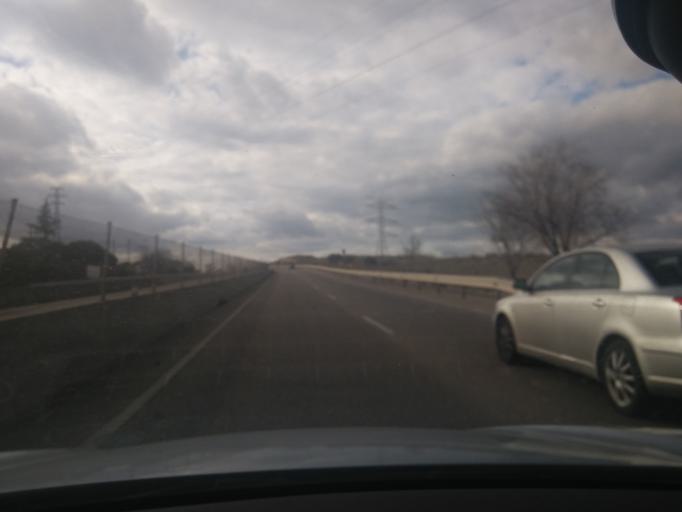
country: ES
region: Madrid
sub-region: Provincia de Madrid
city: Alcobendas
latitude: 40.5529
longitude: -3.6749
